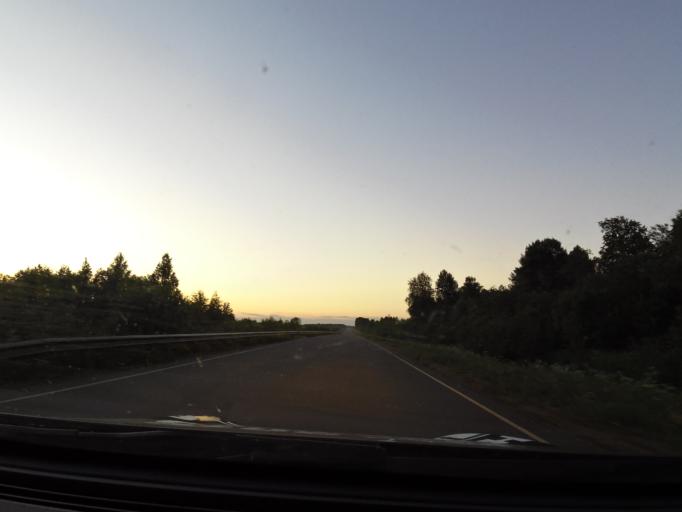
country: RU
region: Vologda
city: Vytegra
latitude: 60.9739
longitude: 36.0970
